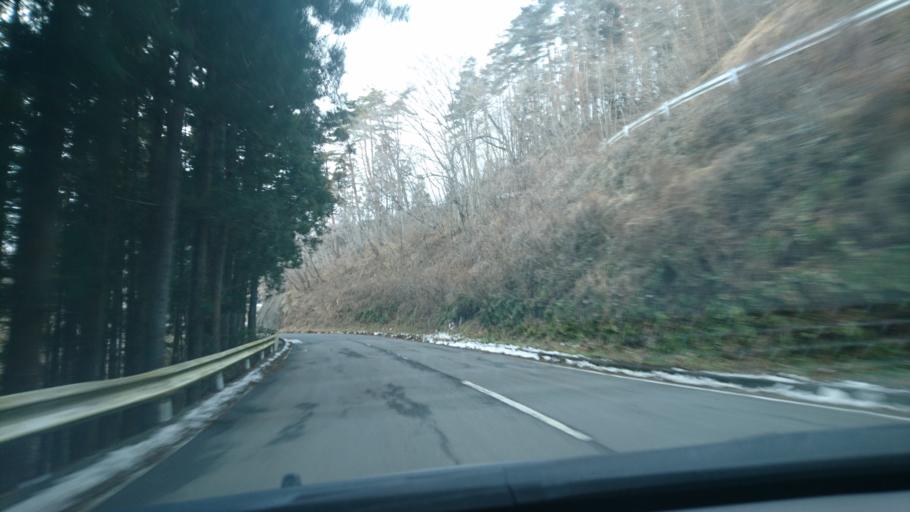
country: JP
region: Iwate
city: Ofunato
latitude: 38.9121
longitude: 141.5130
